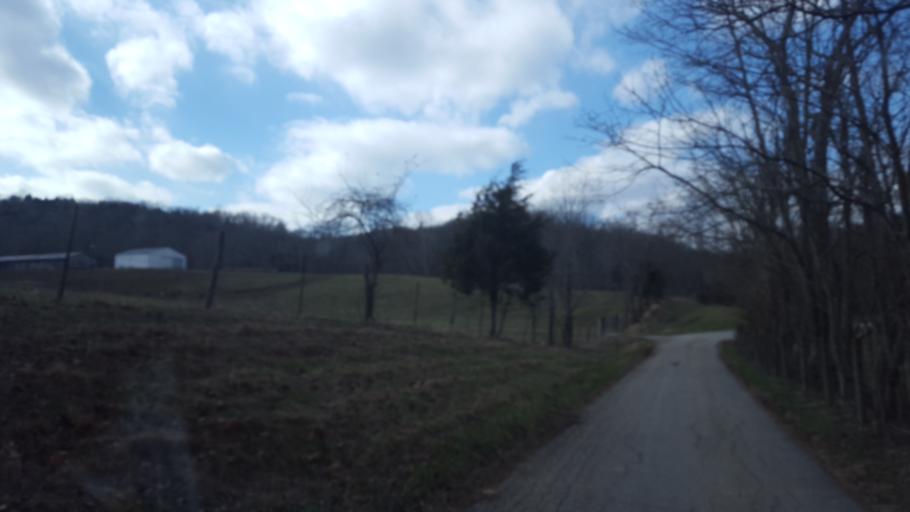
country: US
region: Kentucky
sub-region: Franklin County
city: Frankfort
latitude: 38.3691
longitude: -84.8873
